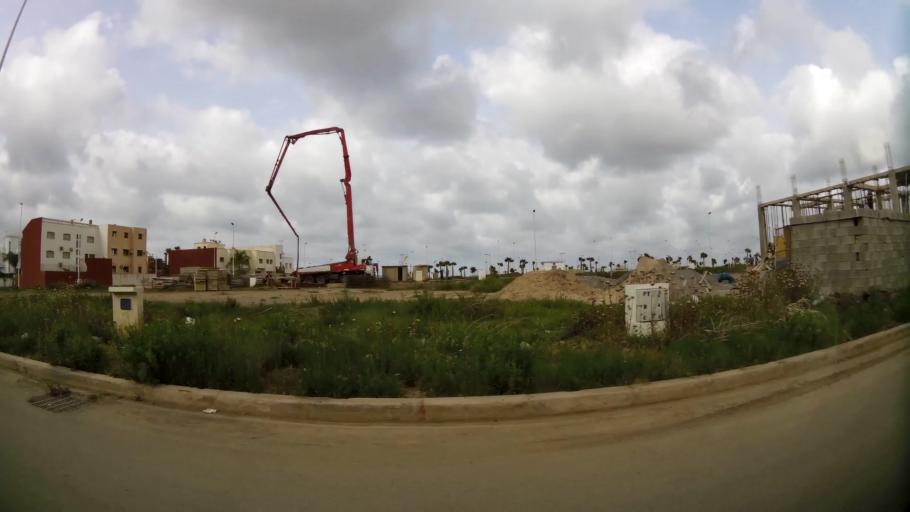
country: MA
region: Oriental
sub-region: Nador
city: Nador
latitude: 35.1658
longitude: -2.9141
